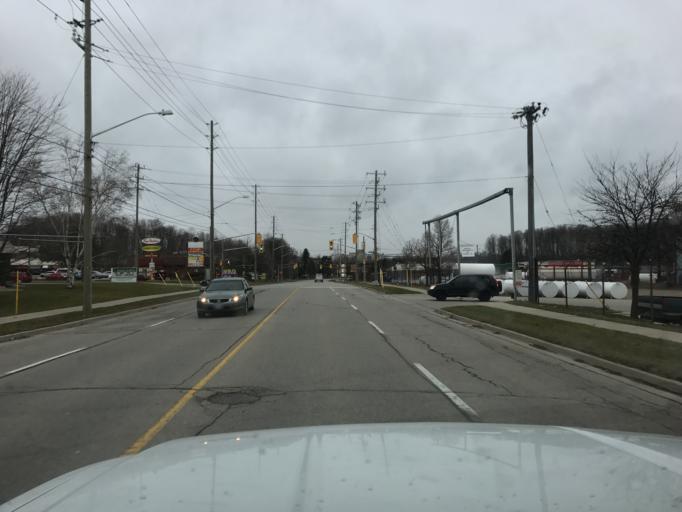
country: CA
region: Ontario
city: Waterloo
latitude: 43.4838
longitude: -80.5391
